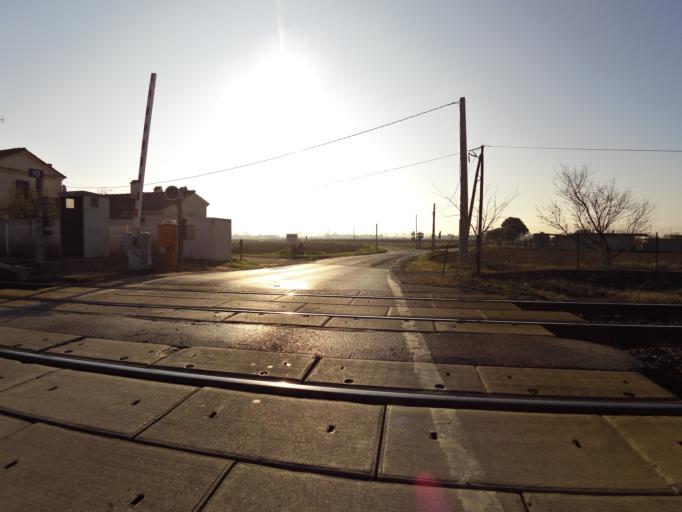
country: FR
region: Languedoc-Roussillon
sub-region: Departement du Gard
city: Mus
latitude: 43.7265
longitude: 4.1931
